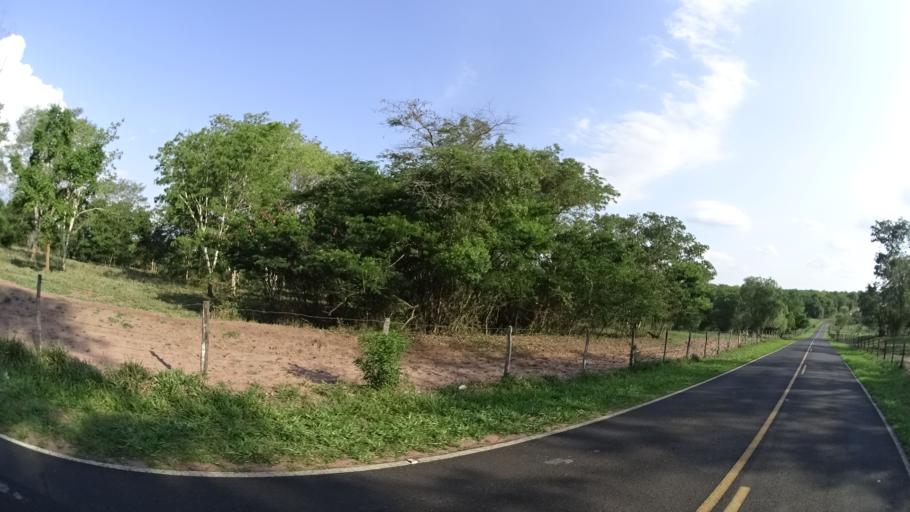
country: BR
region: Sao Paulo
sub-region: Urupes
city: Urupes
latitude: -21.4004
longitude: -49.5157
